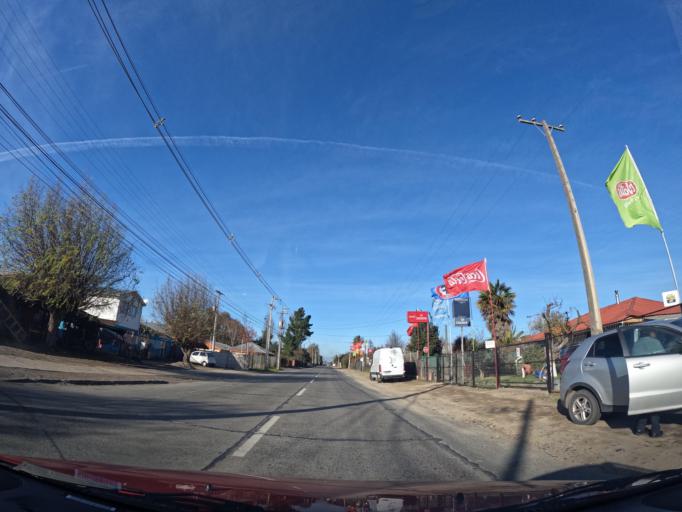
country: CL
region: Maule
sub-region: Provincia de Linares
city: San Javier
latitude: -35.5745
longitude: -71.6716
